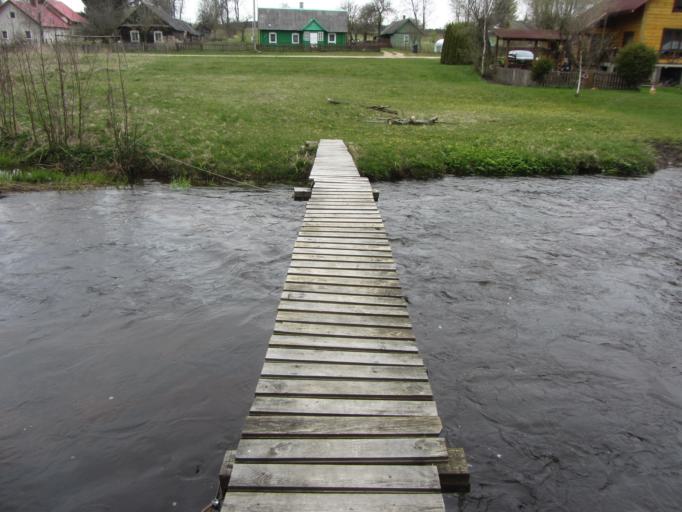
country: LT
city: Skaidiskes
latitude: 54.4590
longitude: 25.4737
